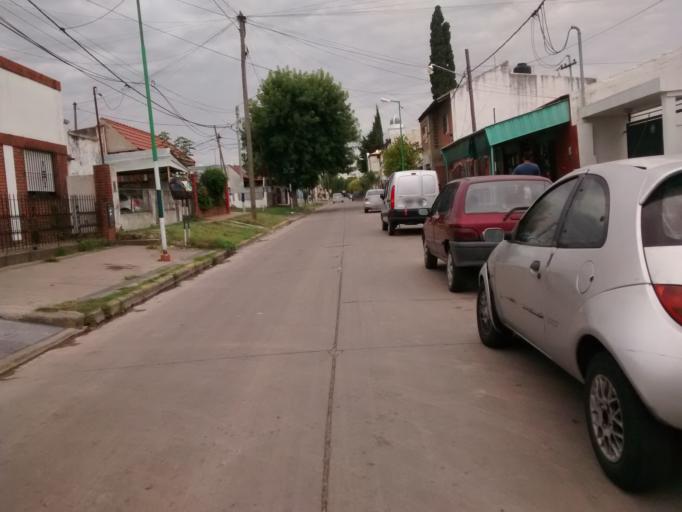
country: AR
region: Buenos Aires
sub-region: Partido de La Plata
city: La Plata
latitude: -34.9404
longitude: -57.9211
